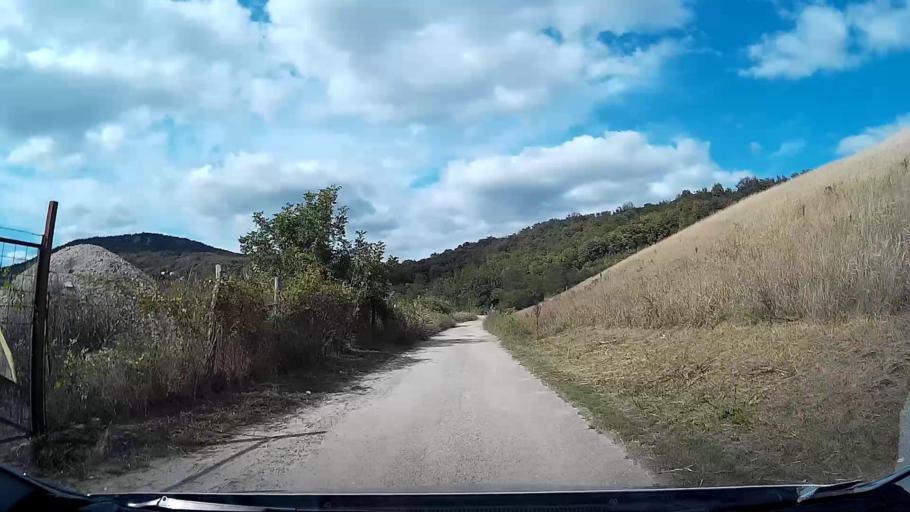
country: HU
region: Pest
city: Nagykovacsi
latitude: 47.6639
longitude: 19.0256
